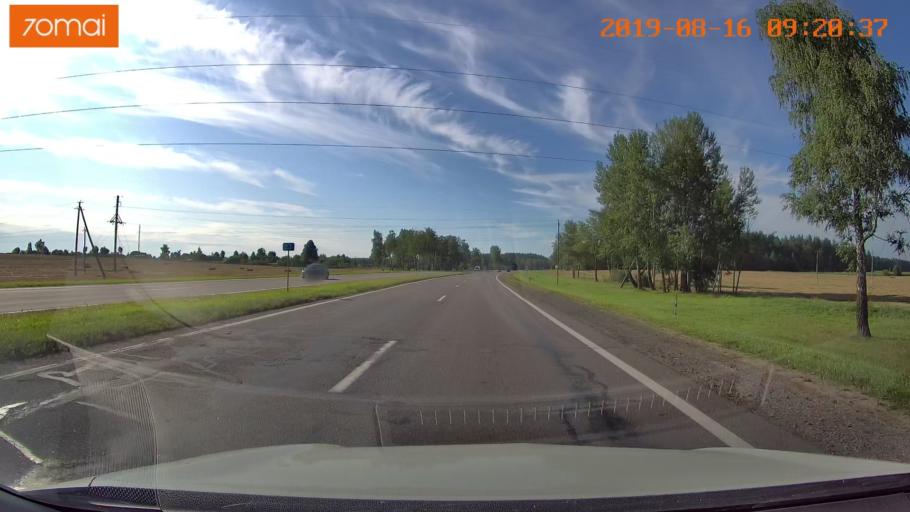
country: BY
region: Minsk
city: Luhavaya Slabada
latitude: 53.7776
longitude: 27.8252
